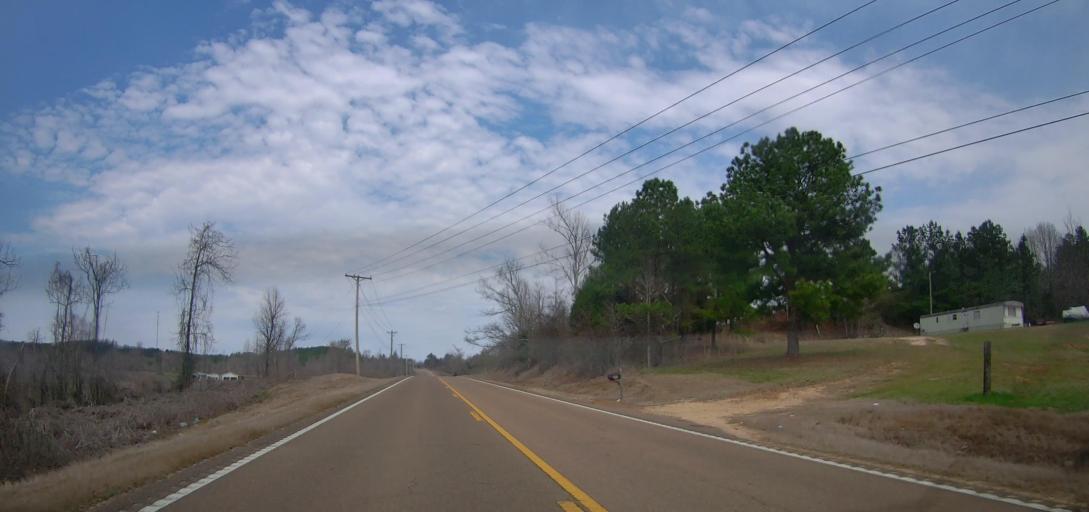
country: US
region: Mississippi
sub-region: Marshall County
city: Holly Springs
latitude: 34.7429
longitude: -89.4258
